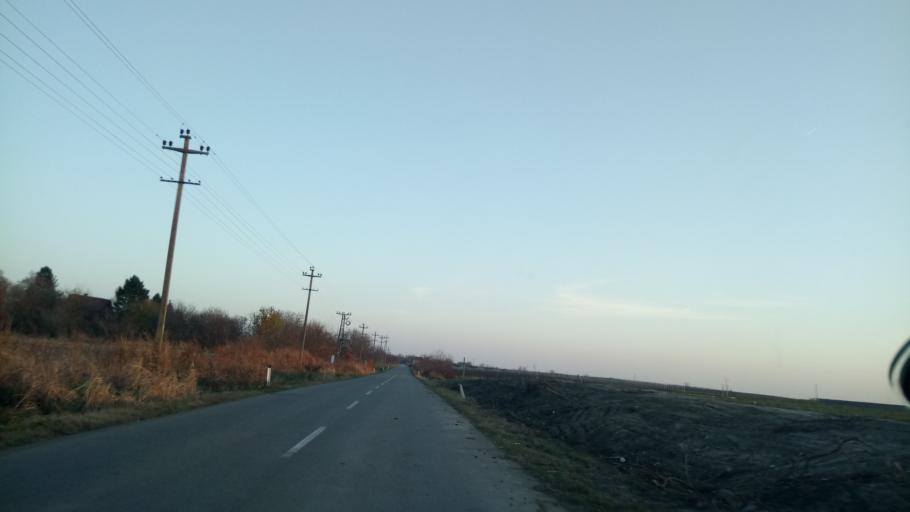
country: RS
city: Surduk
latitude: 45.0893
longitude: 20.3013
